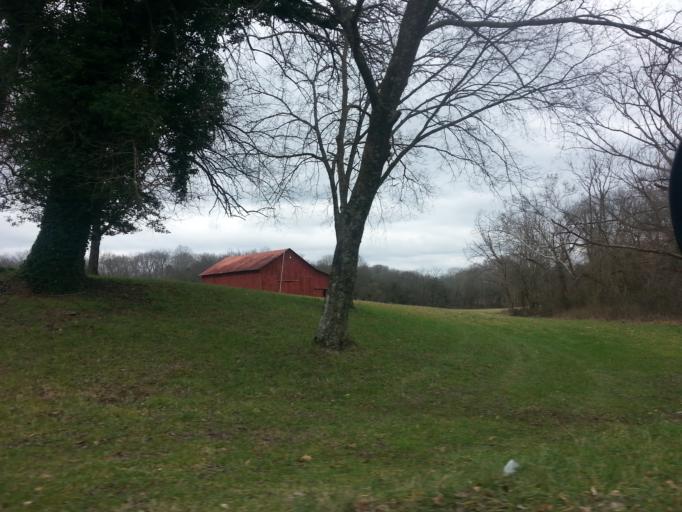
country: US
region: Tennessee
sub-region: Grainger County
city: Blaine
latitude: 36.1595
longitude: -83.6990
